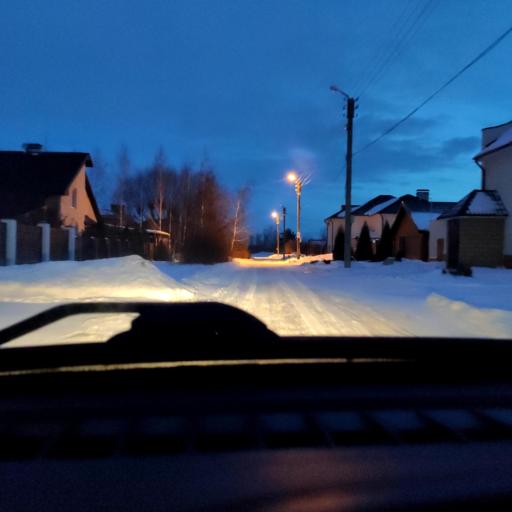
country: RU
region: Samara
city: Tol'yatti
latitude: 53.5561
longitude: 49.3724
